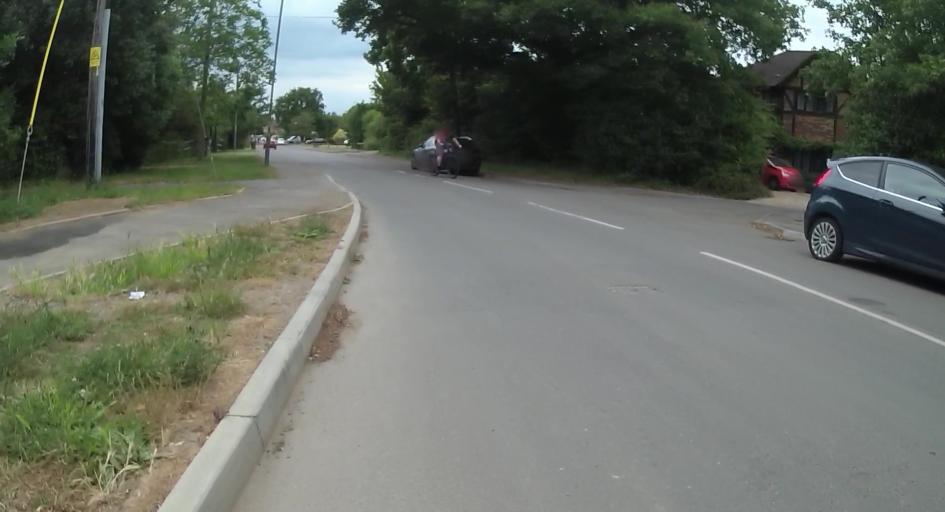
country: GB
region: England
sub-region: Surrey
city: Seale
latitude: 51.2438
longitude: -0.7176
